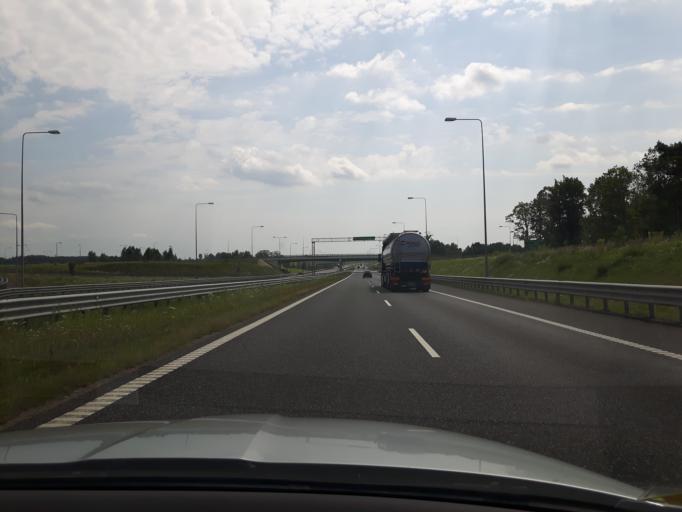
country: PL
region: Warmian-Masurian Voivodeship
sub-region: Powiat olsztynski
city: Olsztynek
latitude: 53.5023
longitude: 20.3108
